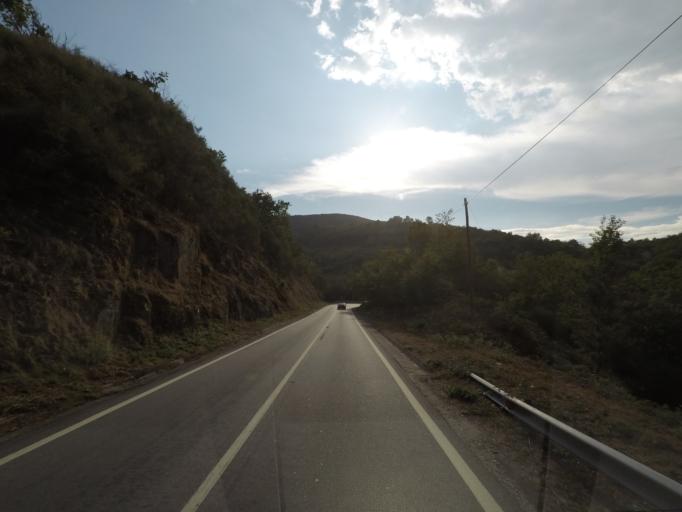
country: PT
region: Porto
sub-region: Baiao
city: Valadares
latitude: 41.2090
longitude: -7.9773
